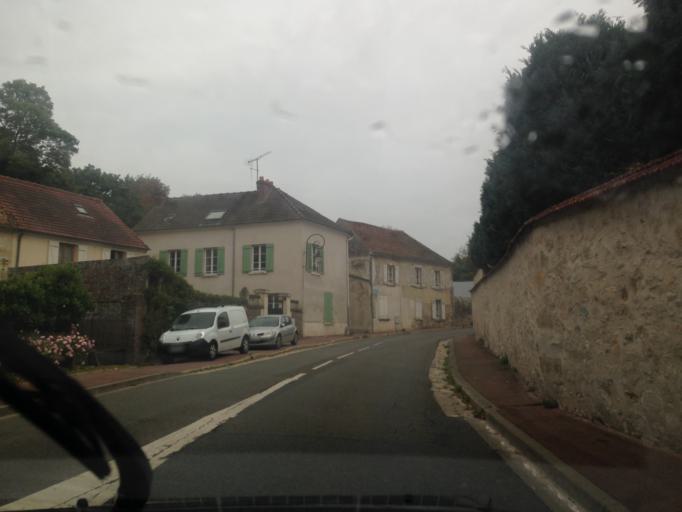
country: FR
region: Ile-de-France
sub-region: Departement du Val-d'Oise
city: Marines
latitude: 49.1303
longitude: 2.0479
